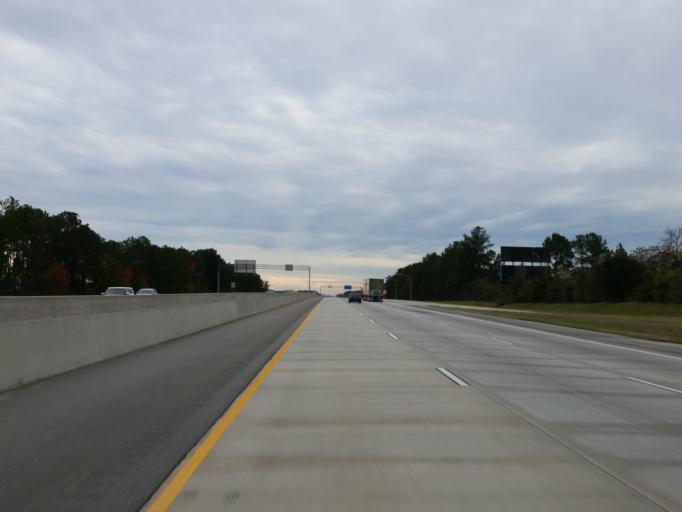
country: US
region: Georgia
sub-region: Cook County
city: Sparks
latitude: 31.2671
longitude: -83.4718
